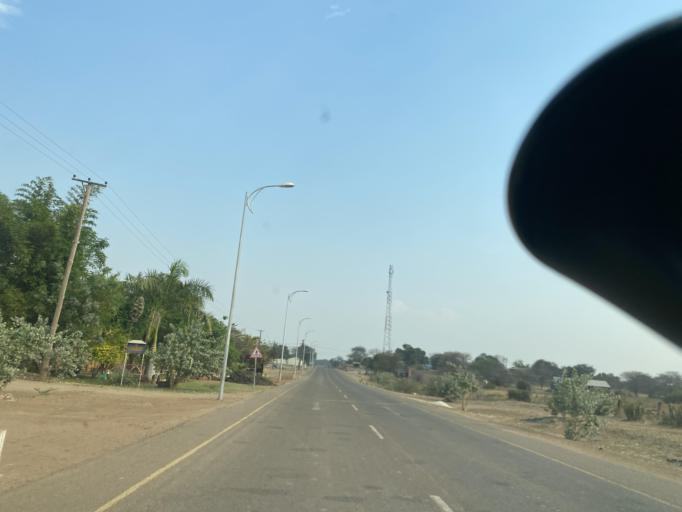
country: ZW
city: Chirundu
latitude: -15.9404
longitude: 28.8736
